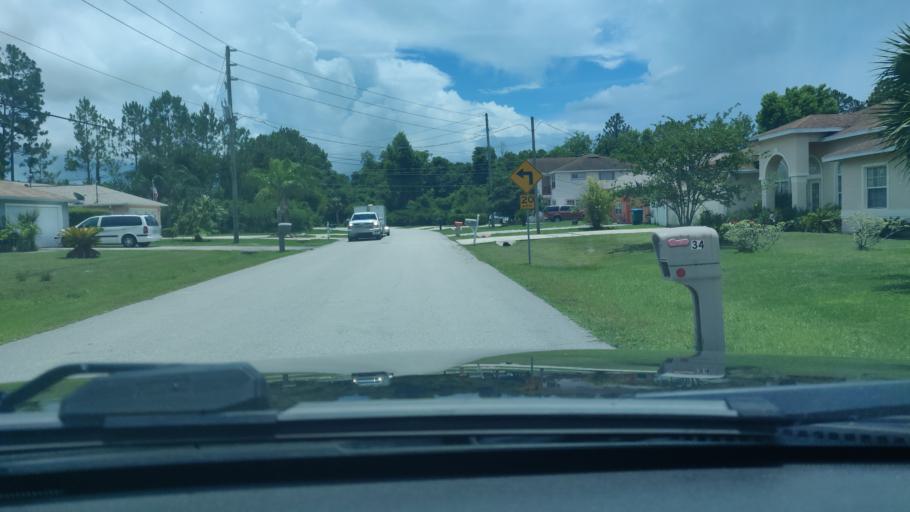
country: US
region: Florida
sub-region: Flagler County
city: Bunnell
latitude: 29.5189
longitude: -81.2563
